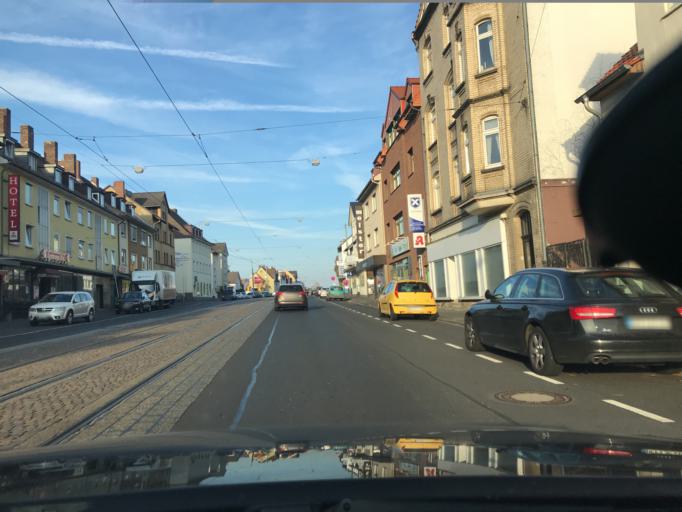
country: DE
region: Hesse
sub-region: Regierungsbezirk Kassel
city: Fuldabruck
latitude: 51.2880
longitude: 9.4707
